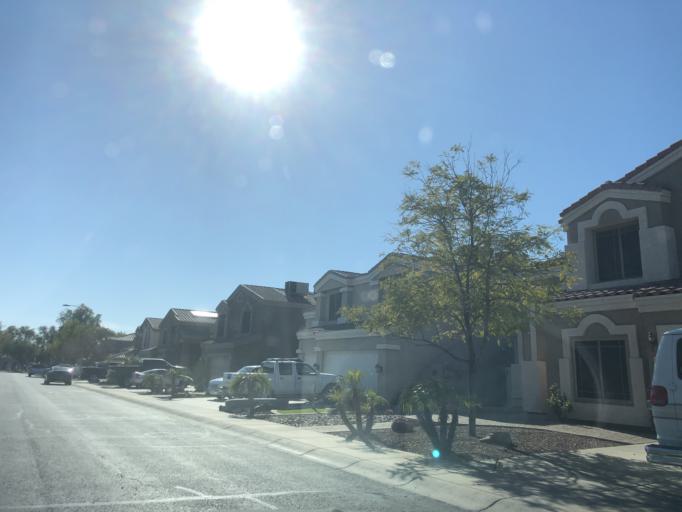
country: US
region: Arizona
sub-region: Maricopa County
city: El Mirage
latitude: 33.6153
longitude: -112.3412
